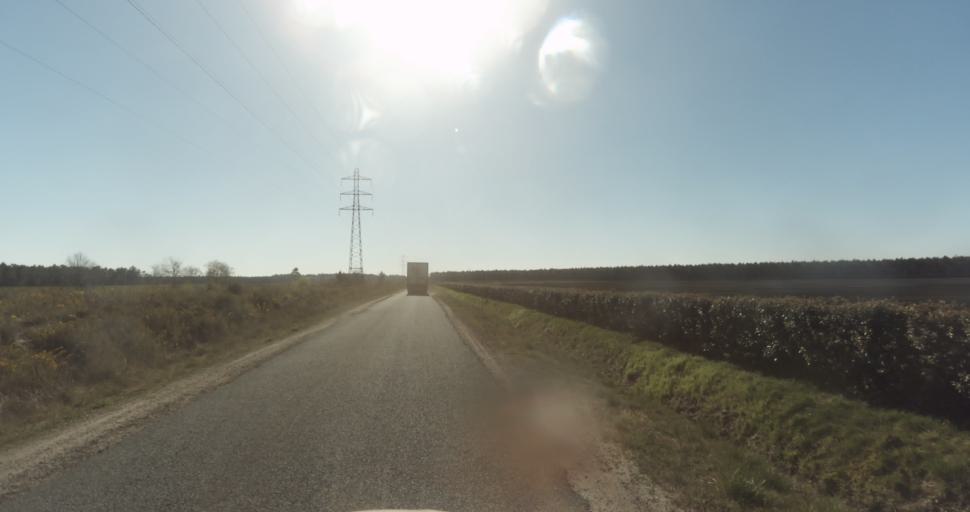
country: FR
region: Aquitaine
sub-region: Departement de la Gironde
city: Marcheprime
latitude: 44.7426
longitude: -0.8269
